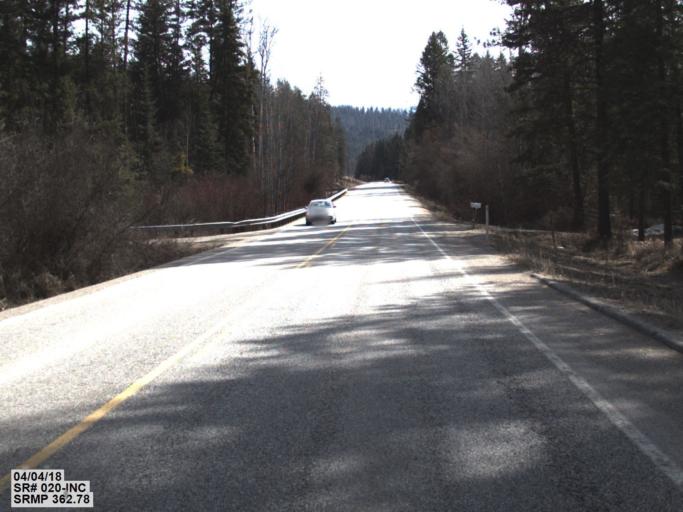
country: US
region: Washington
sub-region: Stevens County
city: Colville
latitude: 48.5156
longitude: -117.7524
